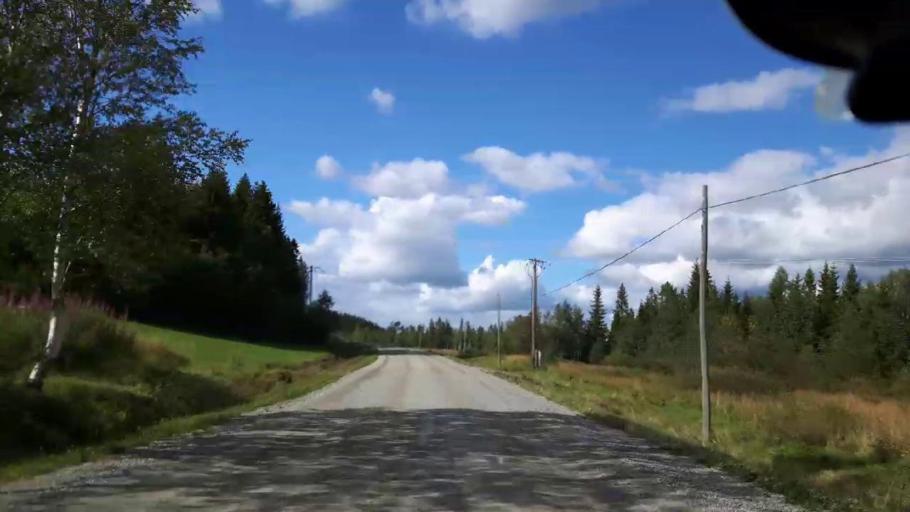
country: SE
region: Jaemtland
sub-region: Stroemsunds Kommun
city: Stroemsund
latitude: 63.3080
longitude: 15.6003
